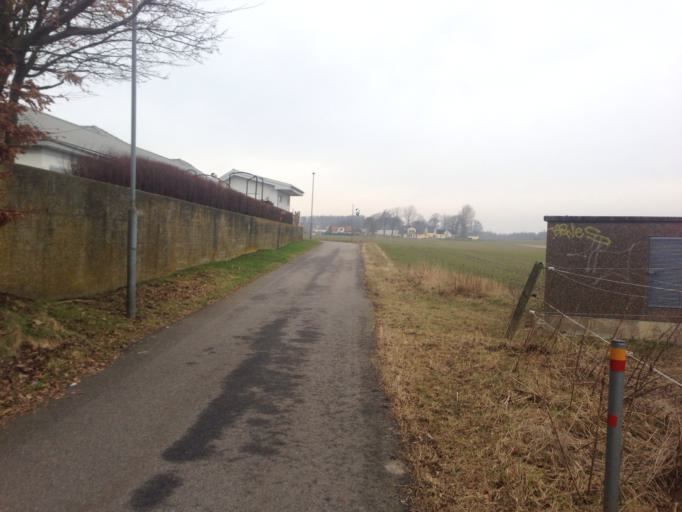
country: SE
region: Skane
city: Bjarred
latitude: 55.7041
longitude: 13.0420
